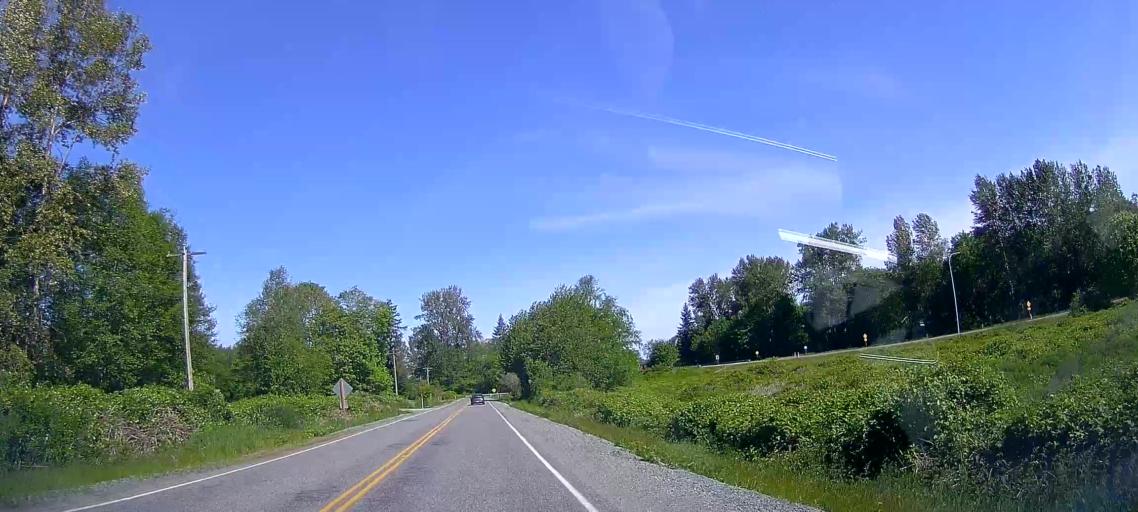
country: US
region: Washington
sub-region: Skagit County
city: Clear Lake
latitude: 48.4811
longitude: -122.2433
